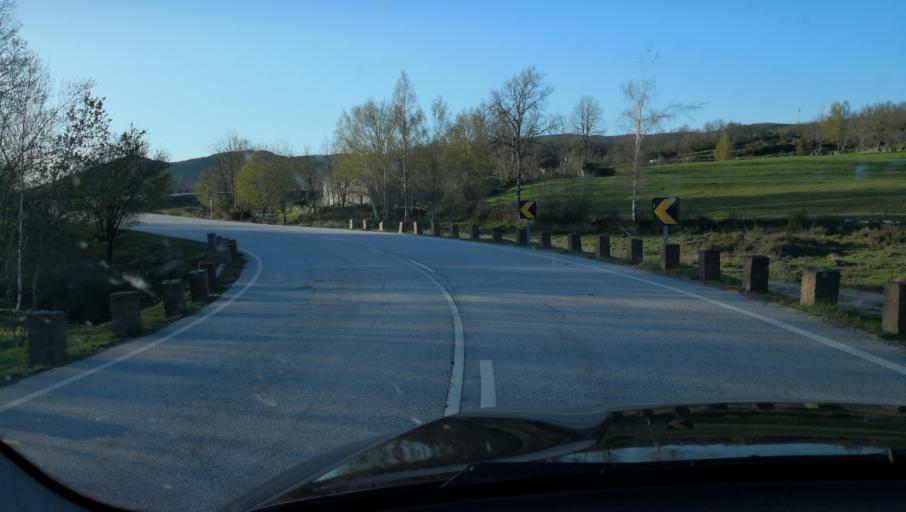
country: PT
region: Vila Real
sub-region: Vila Real
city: Vila Real
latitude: 41.3690
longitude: -7.8013
